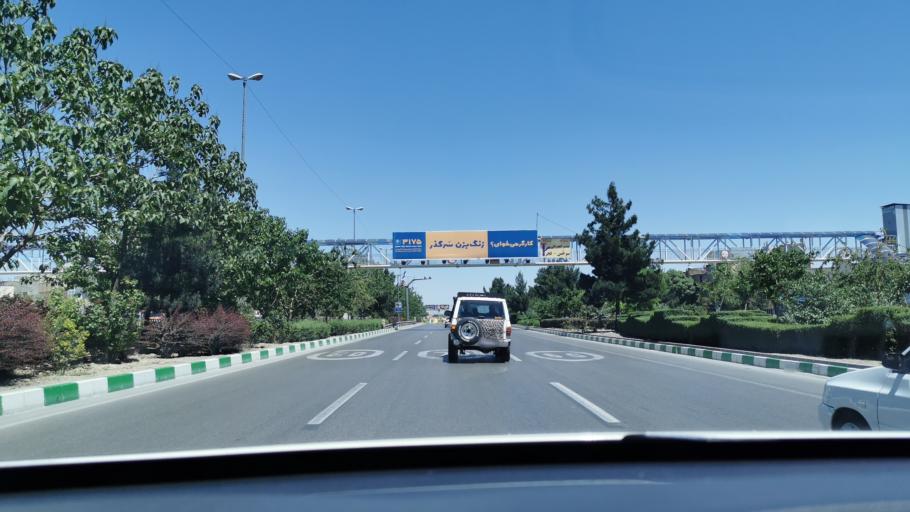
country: IR
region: Razavi Khorasan
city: Mashhad
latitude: 36.2588
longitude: 59.6383
